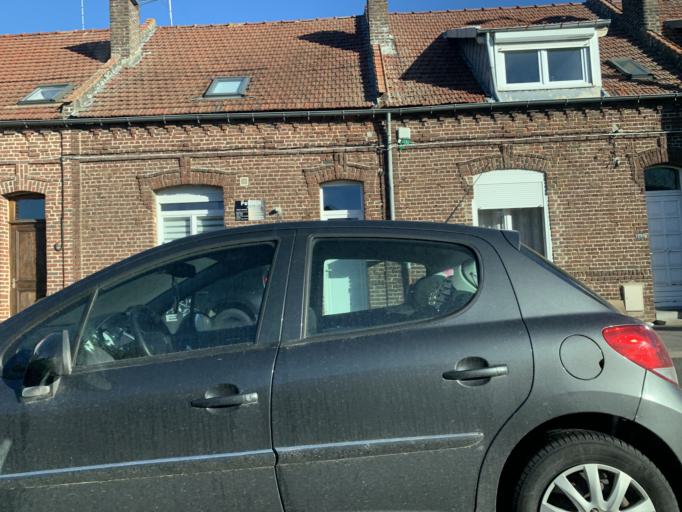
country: FR
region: Nord-Pas-de-Calais
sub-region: Departement du Nord
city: Cambrai
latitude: 50.1681
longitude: 3.2640
